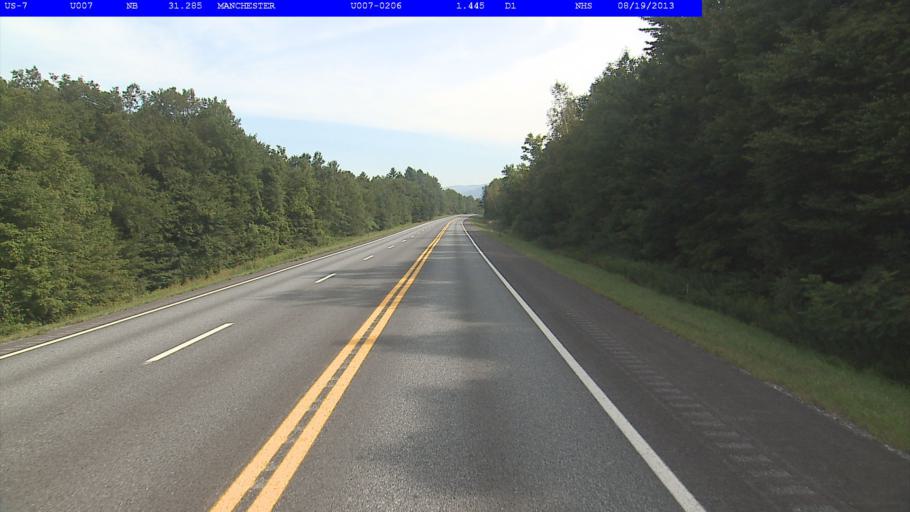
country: US
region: Vermont
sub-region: Bennington County
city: Manchester Center
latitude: 43.1341
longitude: -73.0627
